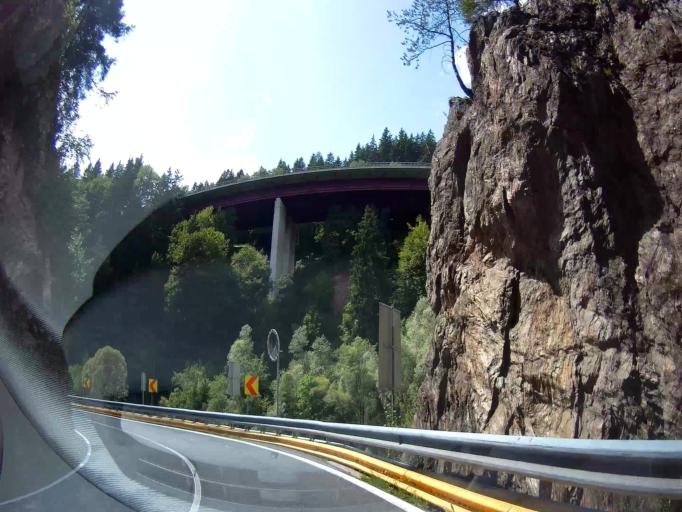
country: AT
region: Carinthia
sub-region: Politischer Bezirk Spittal an der Drau
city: Seeboden
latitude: 46.8433
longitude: 13.5001
